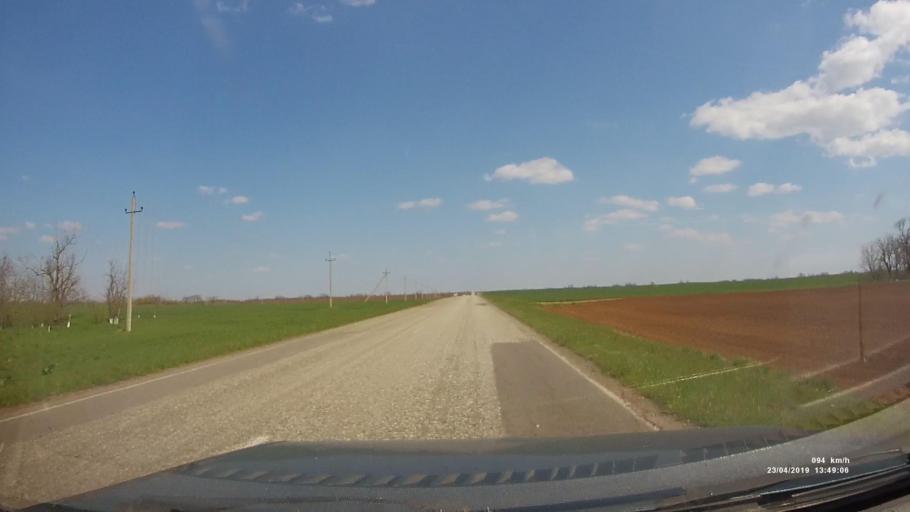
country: RU
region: Kalmykiya
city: Yashalta
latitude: 46.5993
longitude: 42.8865
